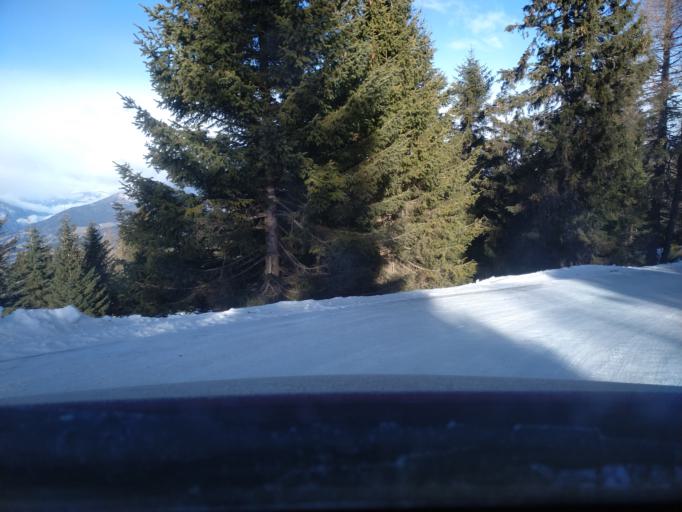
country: AT
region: Carinthia
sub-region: Politischer Bezirk Villach Land
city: Arriach
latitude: 46.6971
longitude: 13.9057
